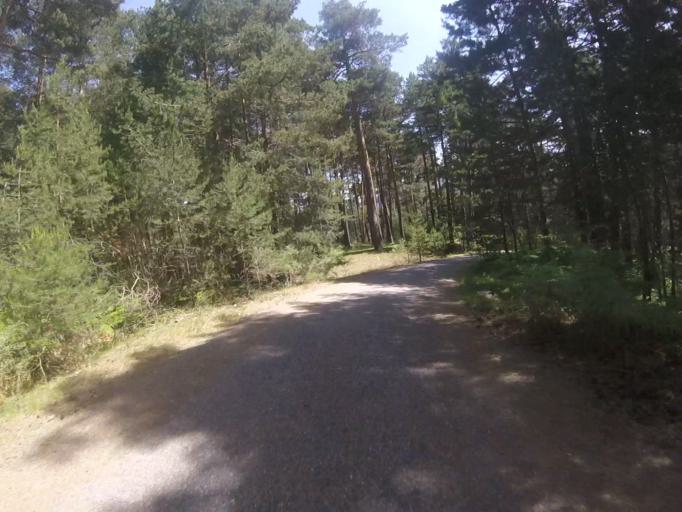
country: ES
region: Madrid
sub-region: Provincia de Madrid
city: Cercedilla
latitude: 40.8083
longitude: -4.0394
